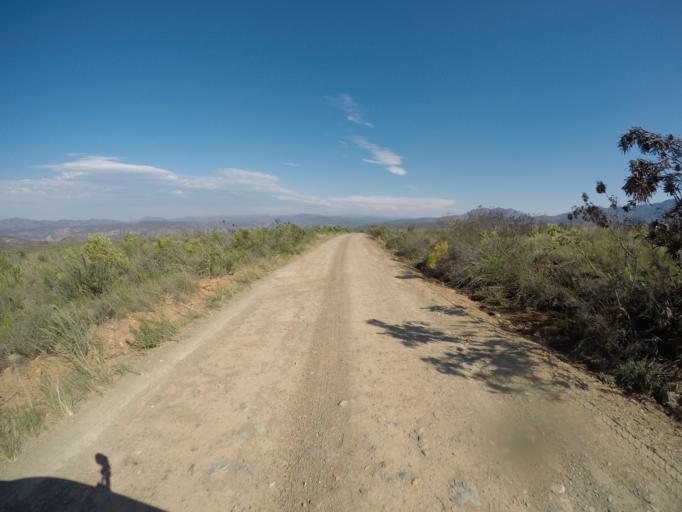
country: ZA
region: Eastern Cape
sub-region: Cacadu District Municipality
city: Kareedouw
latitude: -33.6347
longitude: 24.4741
